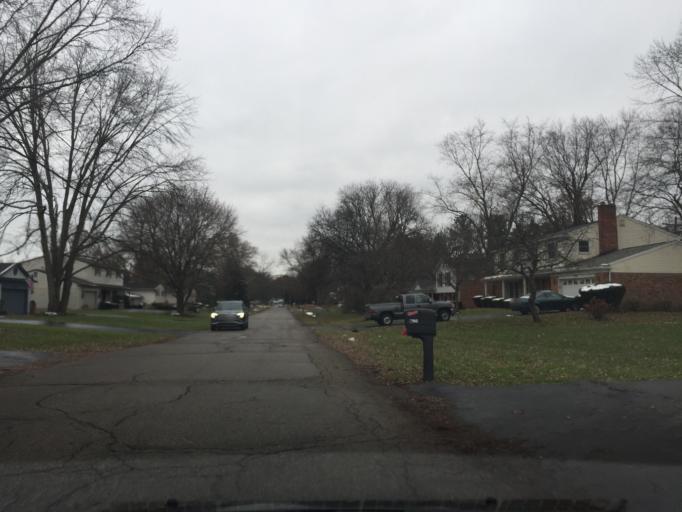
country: US
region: Michigan
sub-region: Oakland County
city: Franklin
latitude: 42.5334
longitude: -83.2911
